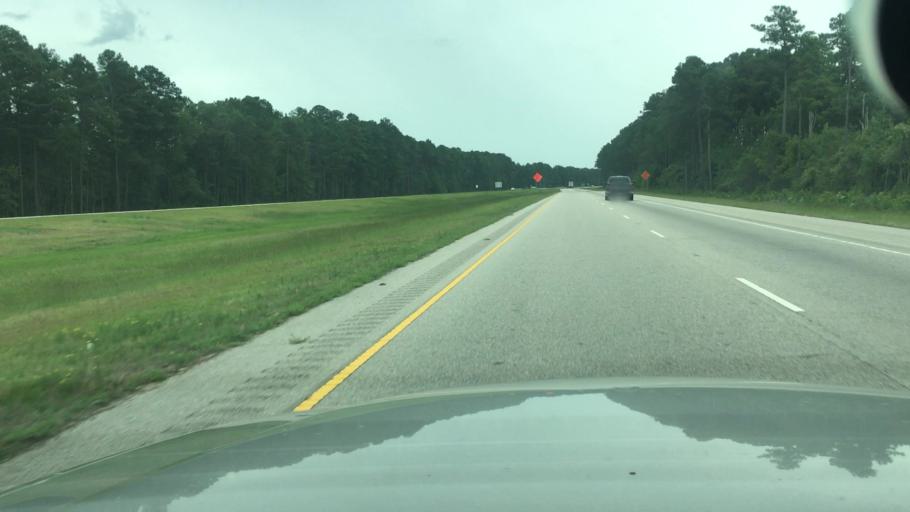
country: US
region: North Carolina
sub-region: Cumberland County
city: Vander
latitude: 34.9678
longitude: -78.8505
